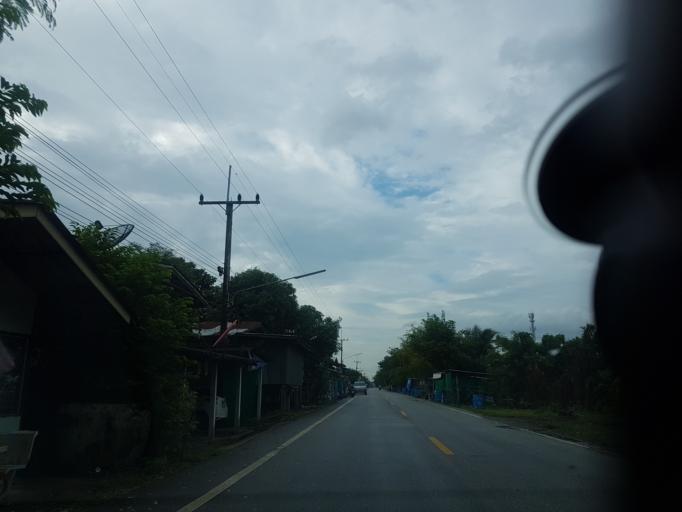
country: TH
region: Pathum Thani
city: Nong Suea
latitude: 14.1549
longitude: 100.8686
